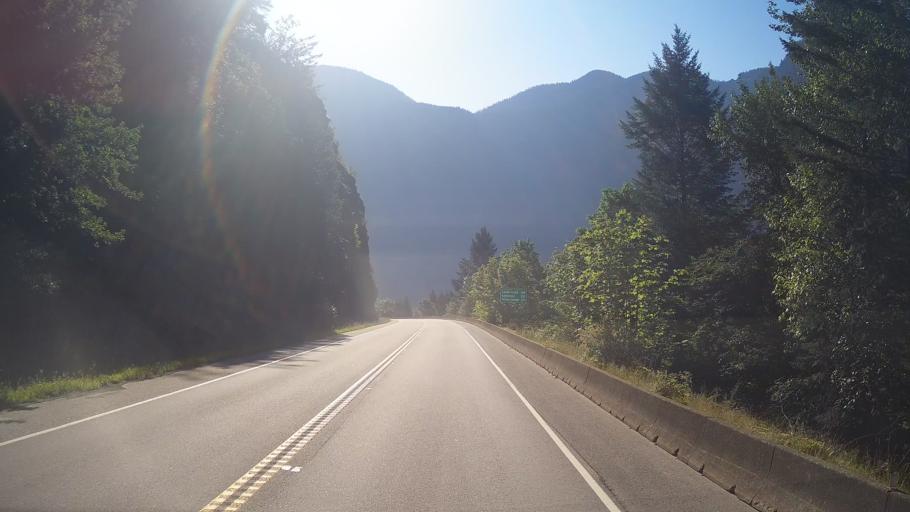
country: CA
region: British Columbia
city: Hope
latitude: 49.5636
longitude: -121.4217
